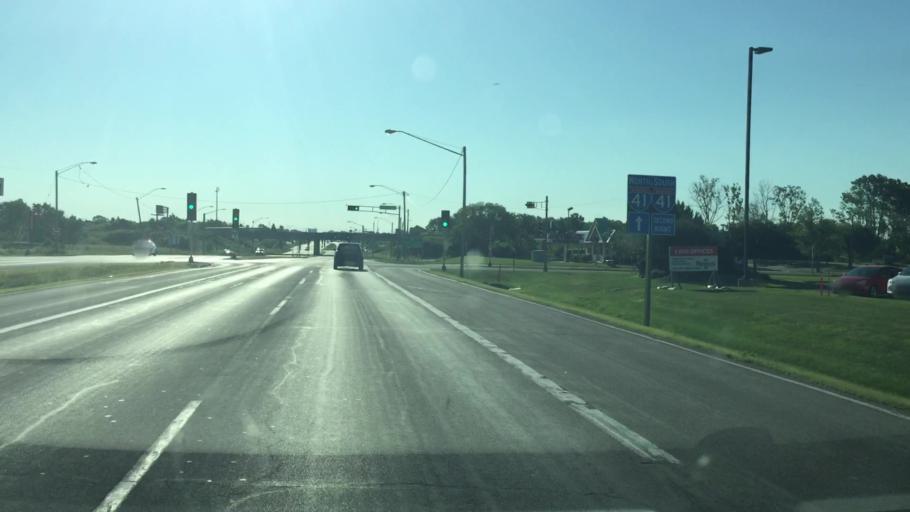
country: US
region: Wisconsin
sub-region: Outagamie County
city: Appleton
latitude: 44.2619
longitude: -88.4704
